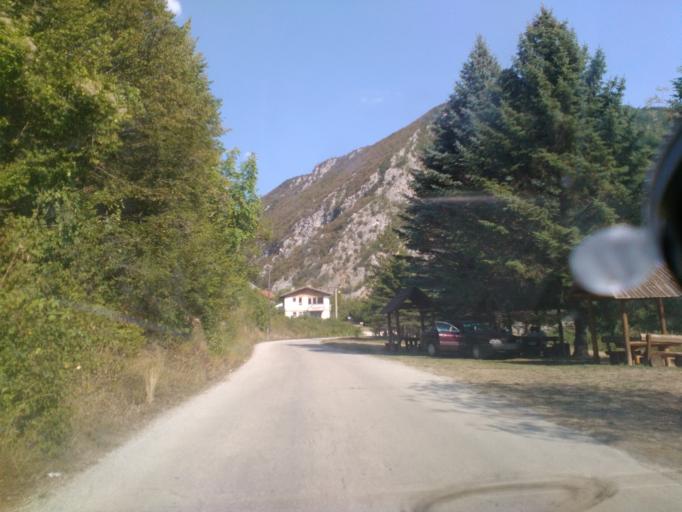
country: BA
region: Federation of Bosnia and Herzegovina
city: Orasac
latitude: 44.4941
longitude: 16.1413
